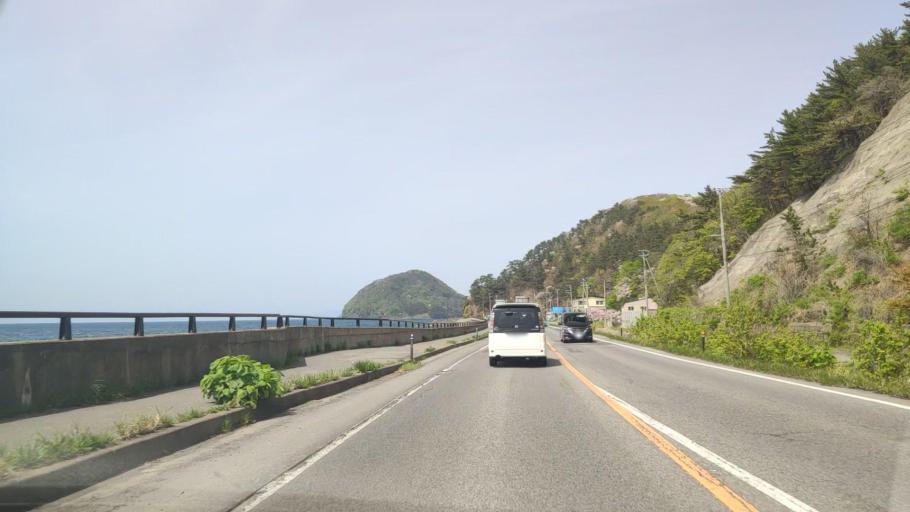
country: JP
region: Aomori
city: Aomori Shi
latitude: 40.8790
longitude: 140.8498
